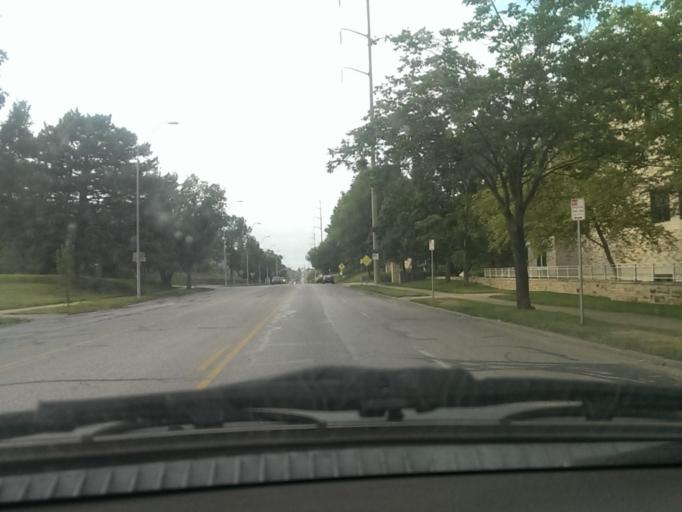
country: US
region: Kansas
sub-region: Johnson County
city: Westwood
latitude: 39.0300
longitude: -94.5736
